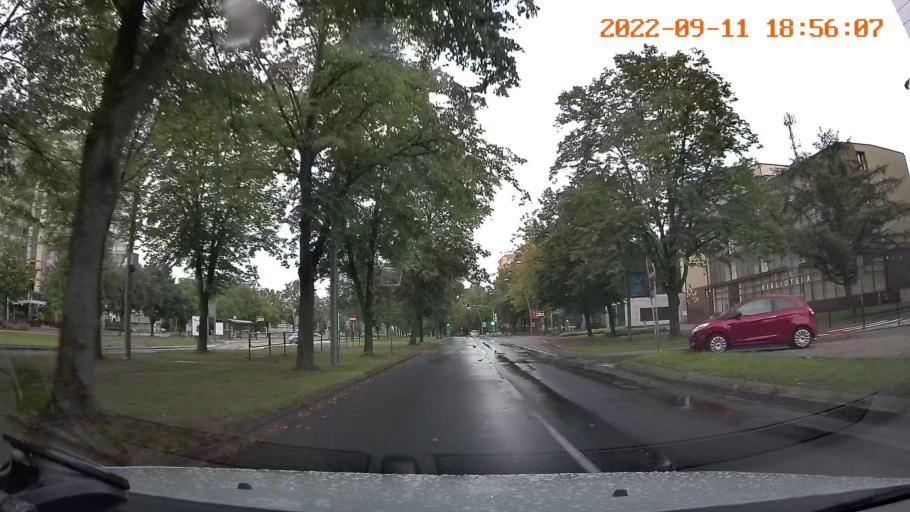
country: PL
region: Silesian Voivodeship
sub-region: Tychy
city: Cielmice
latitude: 50.1143
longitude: 18.9957
